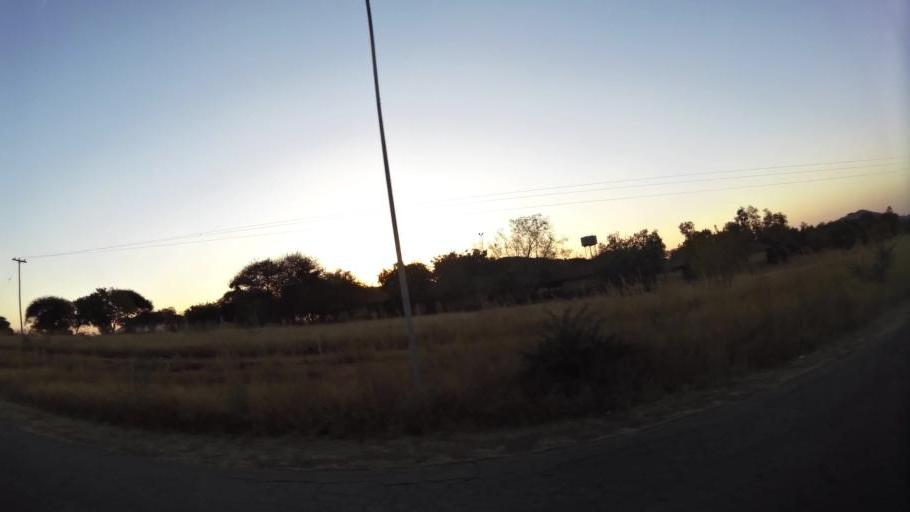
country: ZA
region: North-West
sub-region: Bojanala Platinum District Municipality
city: Rustenburg
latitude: -25.6092
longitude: 27.1788
